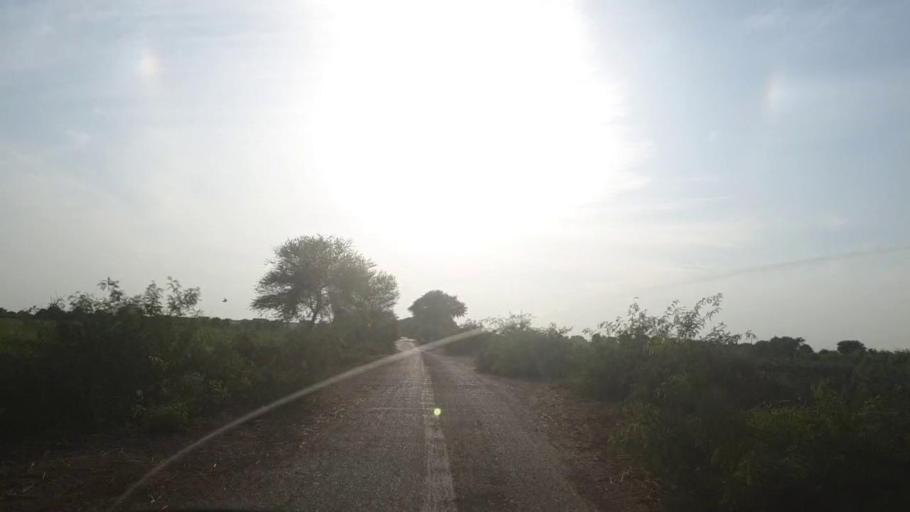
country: PK
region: Sindh
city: Tando Muhammad Khan
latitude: 25.2158
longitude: 68.5169
